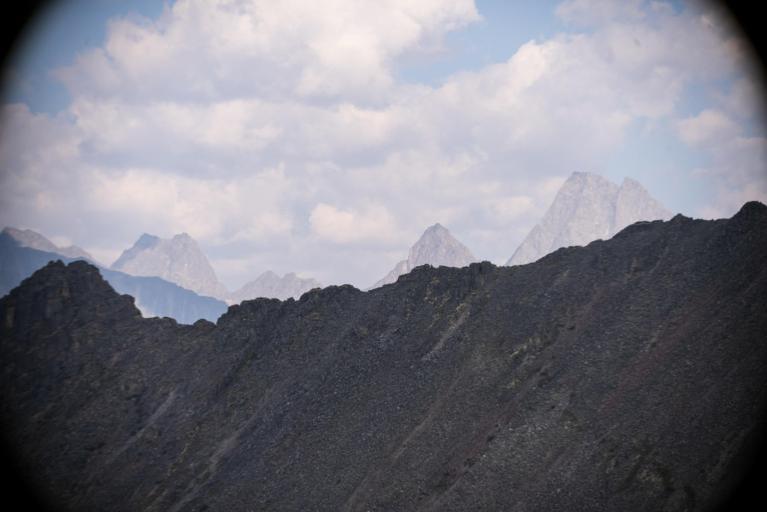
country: RU
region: Transbaikal Territory
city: Chara
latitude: 56.8515
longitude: 117.2033
